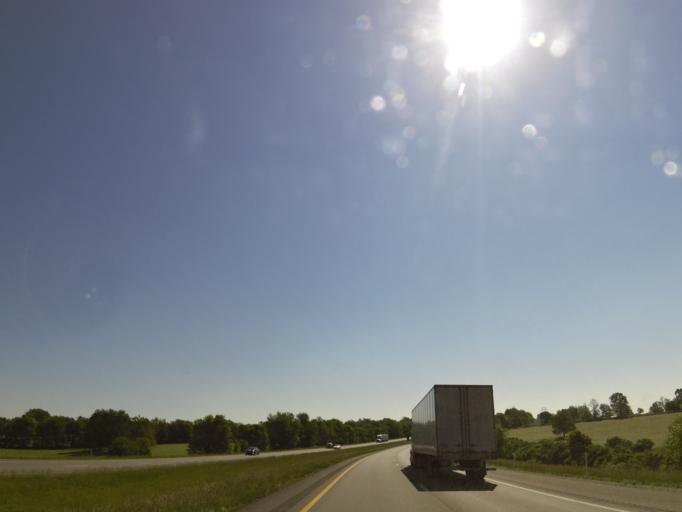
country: US
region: Kentucky
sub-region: Woodford County
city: Midway
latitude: 38.1628
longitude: -84.6333
